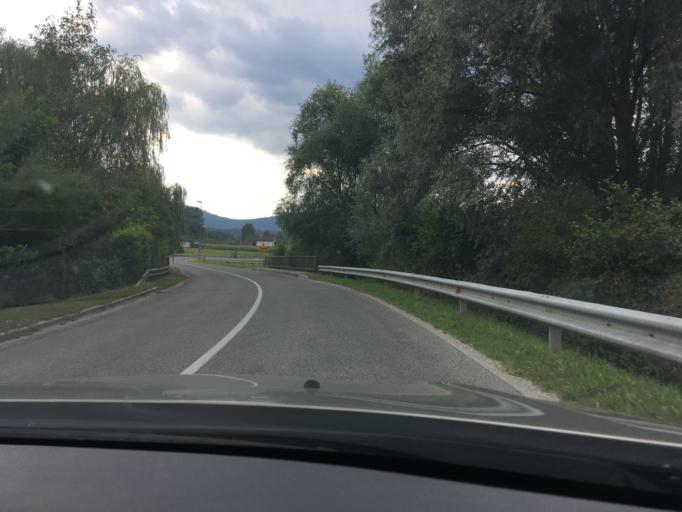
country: SI
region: Straza
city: Straza
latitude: 45.7848
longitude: 15.0999
